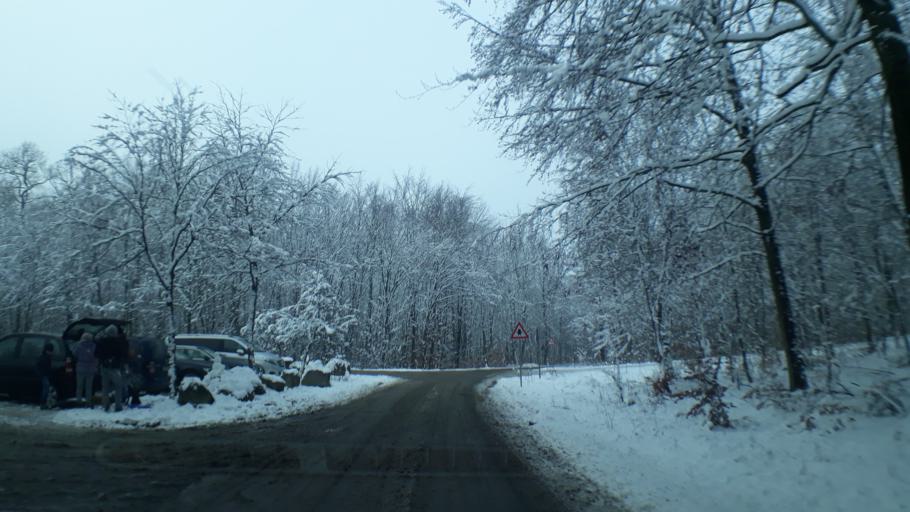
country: DE
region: North Rhine-Westphalia
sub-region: Regierungsbezirk Koln
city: Hurtgenwald
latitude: 50.7426
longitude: 6.3021
